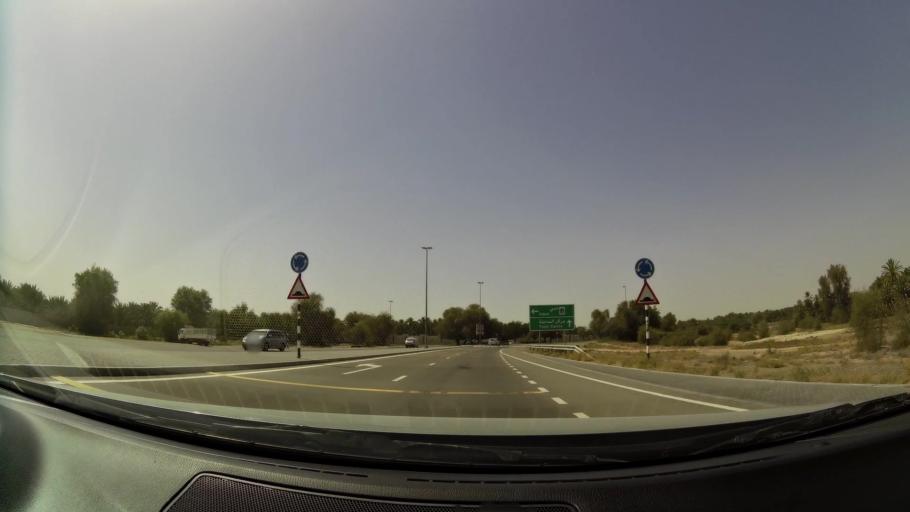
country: OM
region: Al Buraimi
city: Al Buraymi
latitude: 24.2970
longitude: 55.7674
